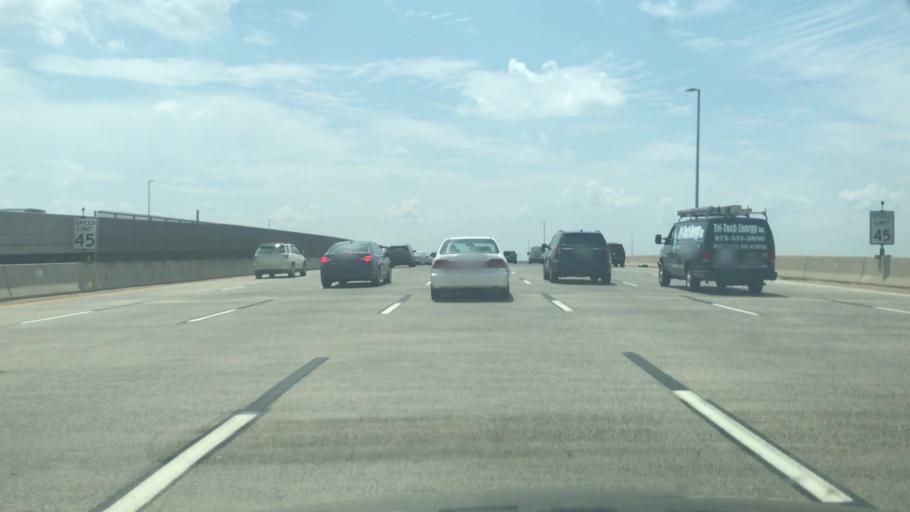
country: US
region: New Jersey
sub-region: Middlesex County
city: Fords
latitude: 40.5116
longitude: -74.3012
